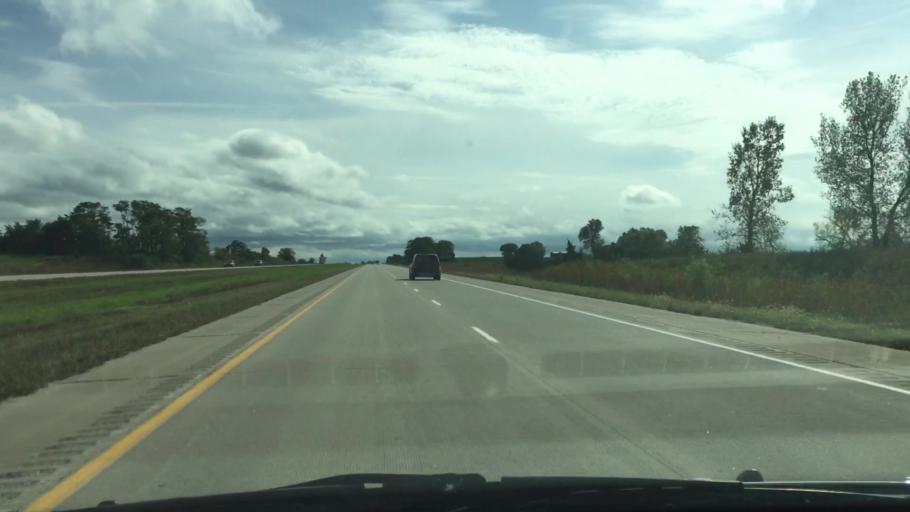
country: US
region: Iowa
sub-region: Decatur County
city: Leon
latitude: 40.8579
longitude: -93.8036
